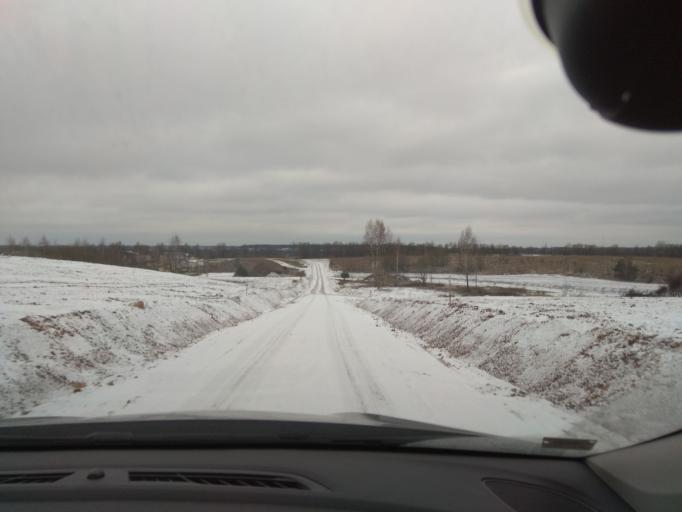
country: LT
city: Lentvaris
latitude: 54.6478
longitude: 25.0830
